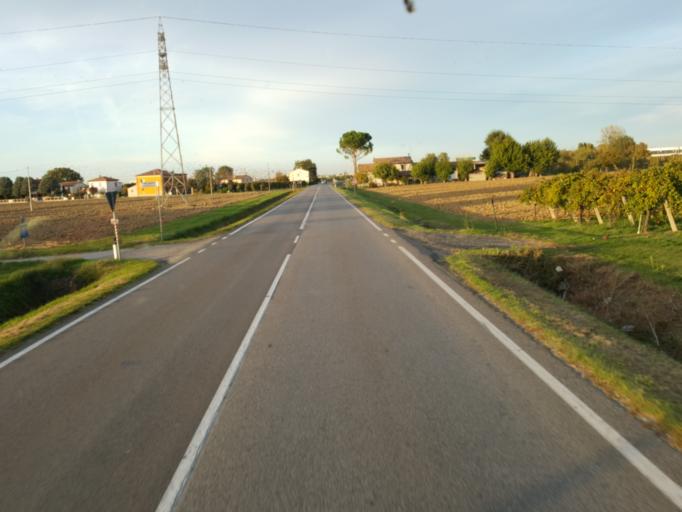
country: IT
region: Emilia-Romagna
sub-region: Provincia di Ravenna
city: Faenza
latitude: 44.3051
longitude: 11.8859
